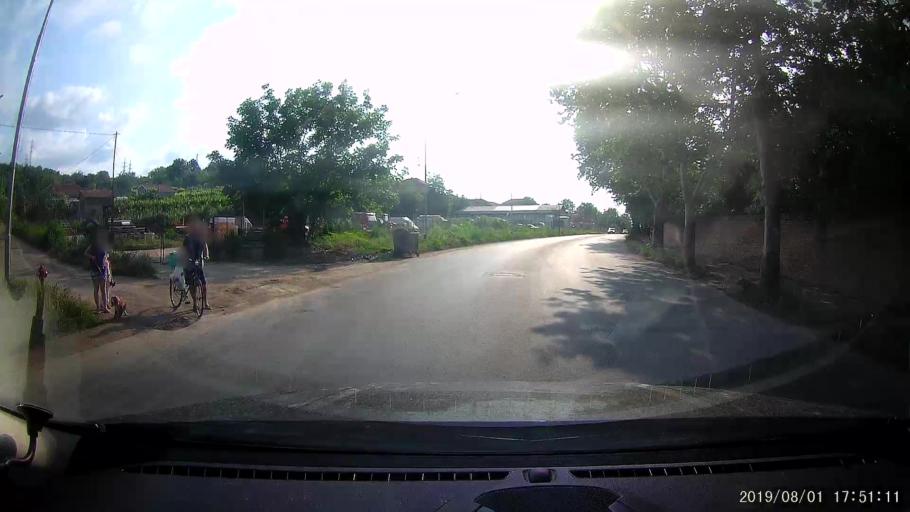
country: BG
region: Silistra
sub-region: Obshtina Silistra
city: Silistra
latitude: 44.1077
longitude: 27.2572
